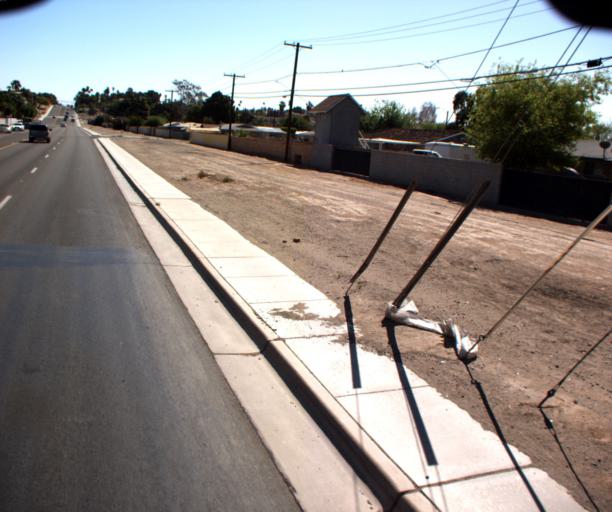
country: US
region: Arizona
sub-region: Yuma County
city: Yuma
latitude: 32.6984
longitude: -114.6461
